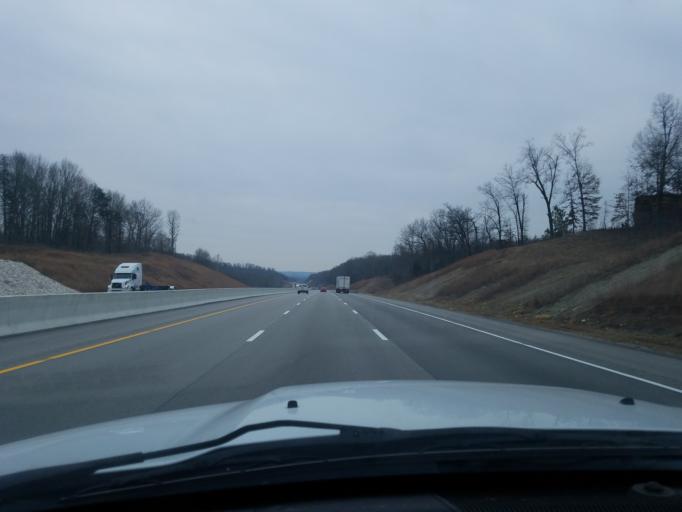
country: US
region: Kentucky
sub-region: Hart County
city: Munfordville
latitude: 37.3230
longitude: -85.9062
